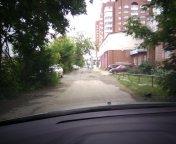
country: RU
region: Sverdlovsk
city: Sovkhoznyy
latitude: 56.7663
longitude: 60.6054
